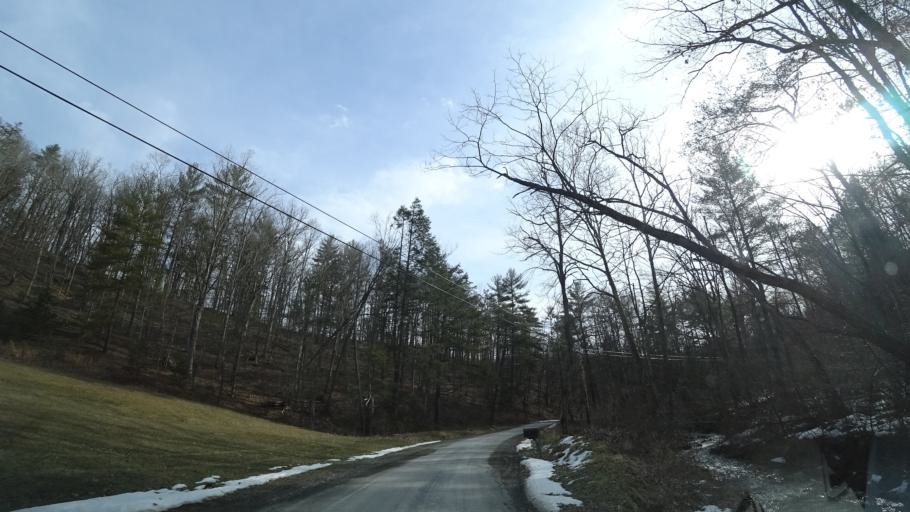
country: US
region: West Virginia
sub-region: Hardy County
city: Moorefield
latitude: 39.0220
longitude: -78.7724
